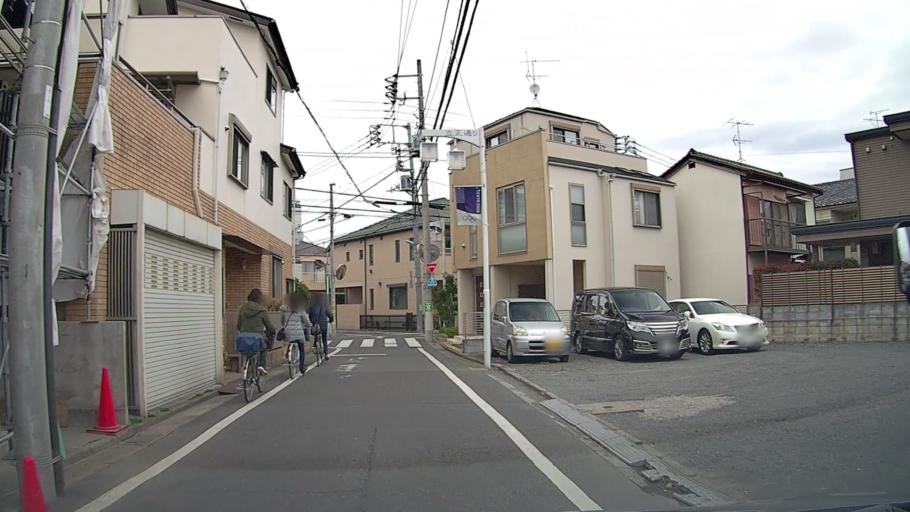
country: JP
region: Tokyo
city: Tokyo
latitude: 35.6915
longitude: 139.6449
